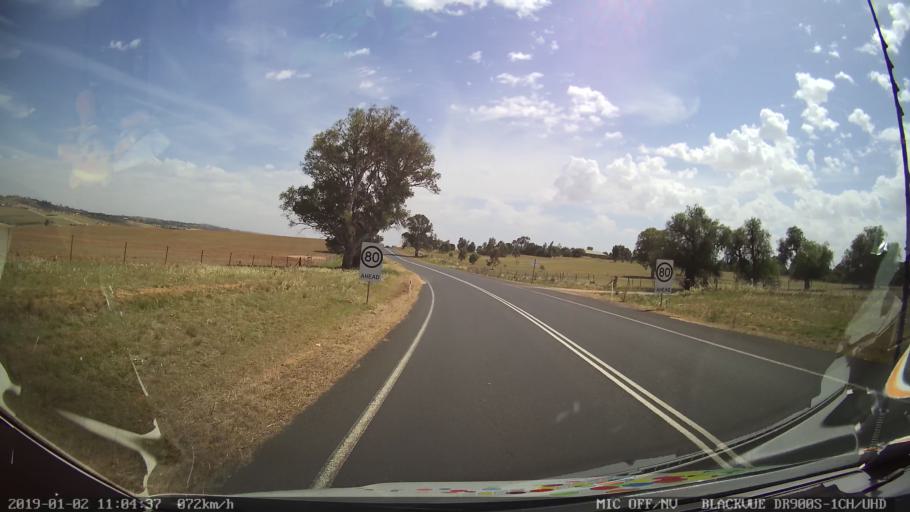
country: AU
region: New South Wales
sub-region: Young
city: Young
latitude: -34.5740
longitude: 148.3533
